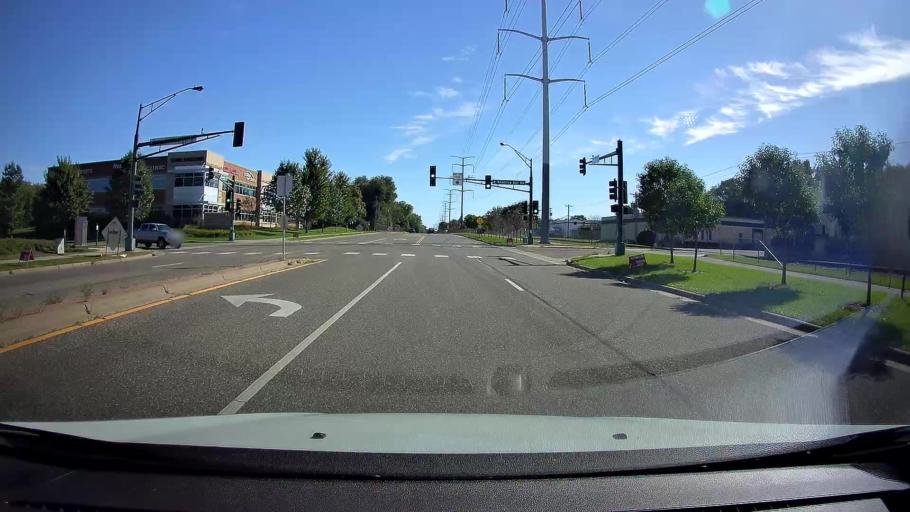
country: US
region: Minnesota
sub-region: Ramsey County
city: Roseville
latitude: 45.0209
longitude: -93.1636
